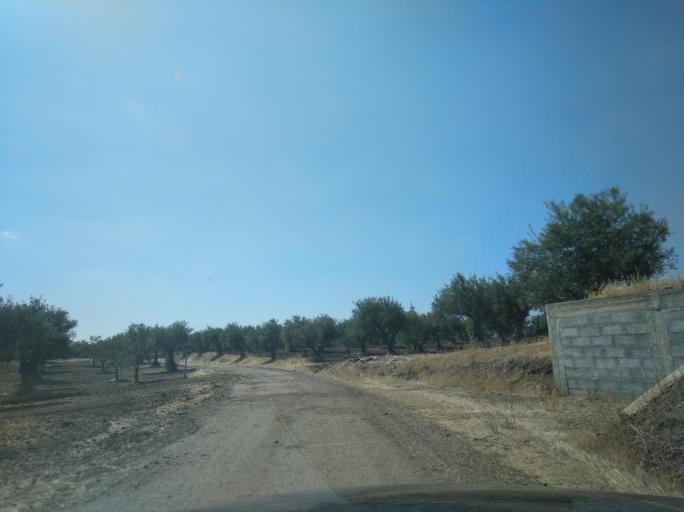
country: PT
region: Portalegre
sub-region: Campo Maior
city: Campo Maior
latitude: 39.0255
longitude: -7.1057
